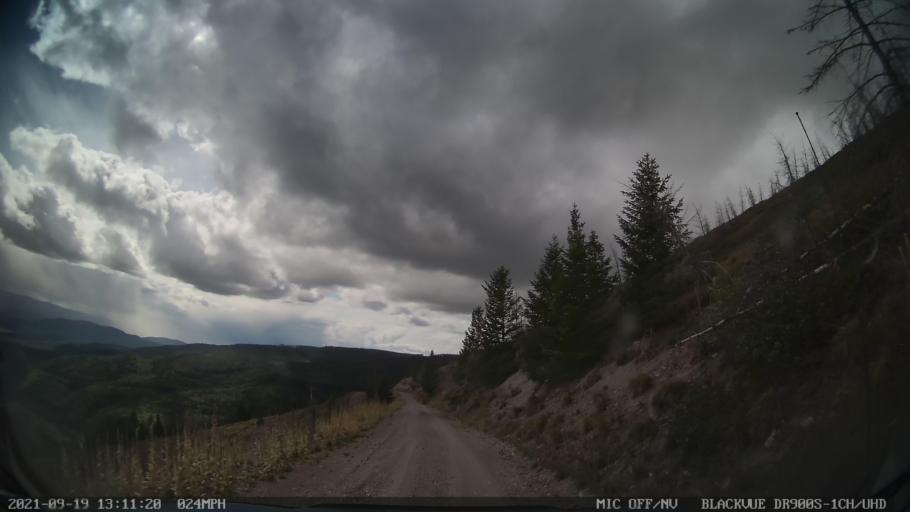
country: US
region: Montana
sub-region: Missoula County
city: Seeley Lake
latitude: 47.1750
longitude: -113.3480
